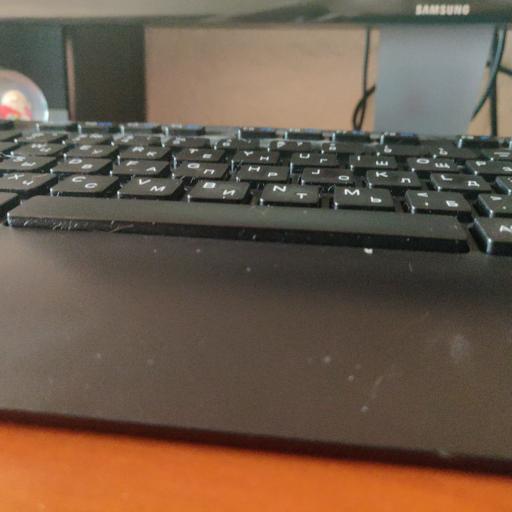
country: FI
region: Haeme
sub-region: Forssa
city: Ypaejae
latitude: 60.7961
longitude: 23.2591
